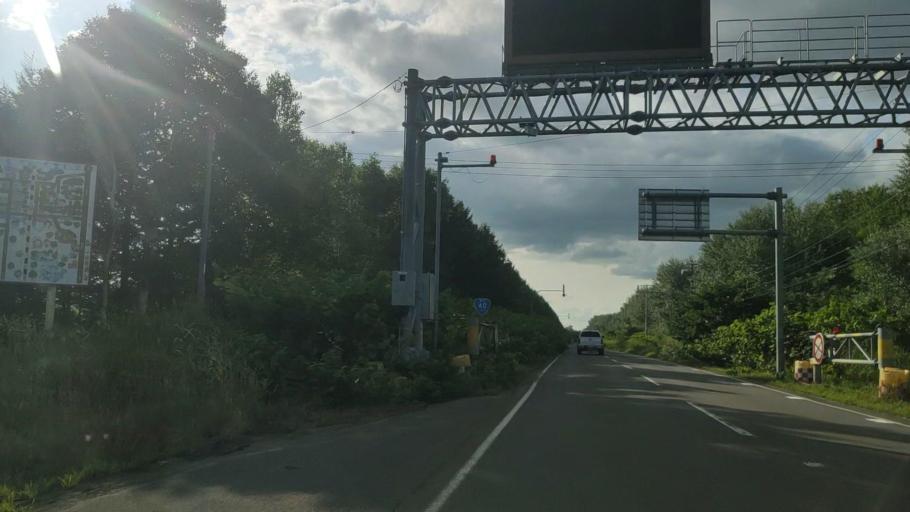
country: JP
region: Hokkaido
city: Makubetsu
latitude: 44.8983
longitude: 141.9154
